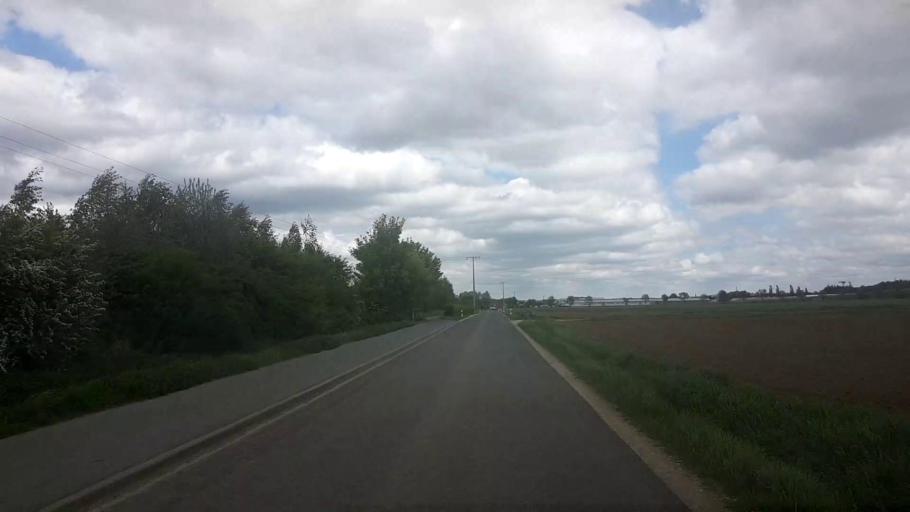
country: DE
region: Bavaria
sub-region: Upper Franconia
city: Bad Staffelstein
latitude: 50.1235
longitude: 11.0164
